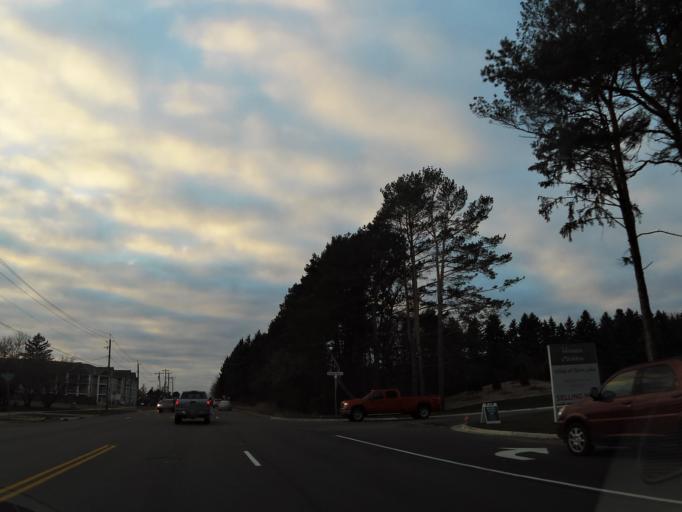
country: US
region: Minnesota
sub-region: Ramsey County
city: Vadnais Heights
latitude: 45.0504
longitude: -93.0449
